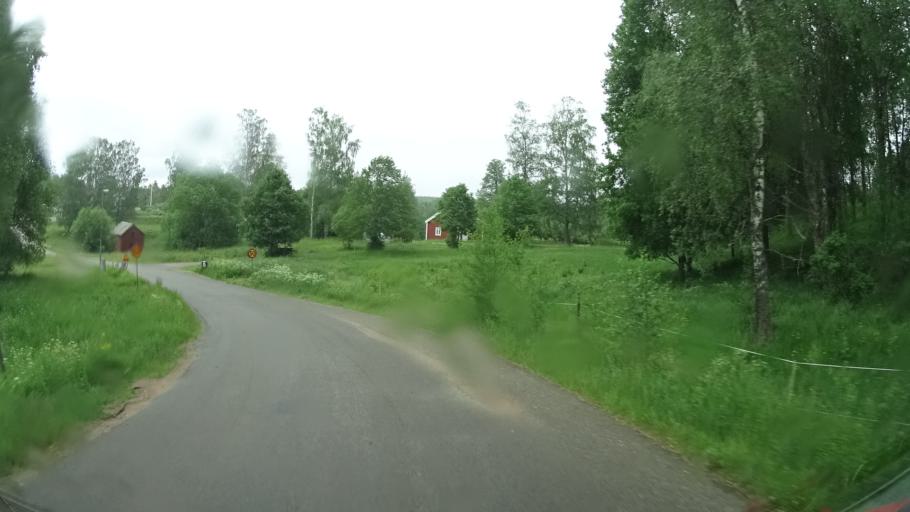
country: SE
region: Joenkoeping
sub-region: Eksjo Kommun
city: Mariannelund
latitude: 57.6761
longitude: 15.5879
